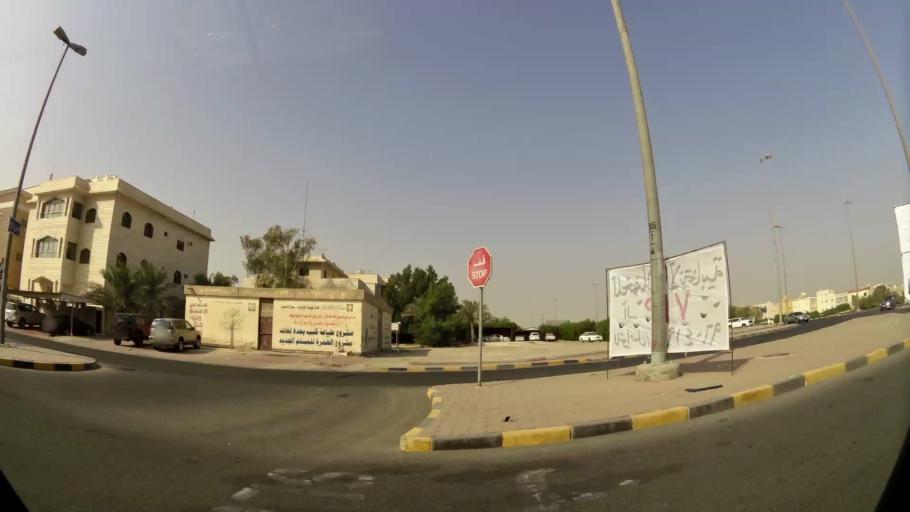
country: KW
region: Al Asimah
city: Ar Rabiyah
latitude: 29.2742
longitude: 47.8699
